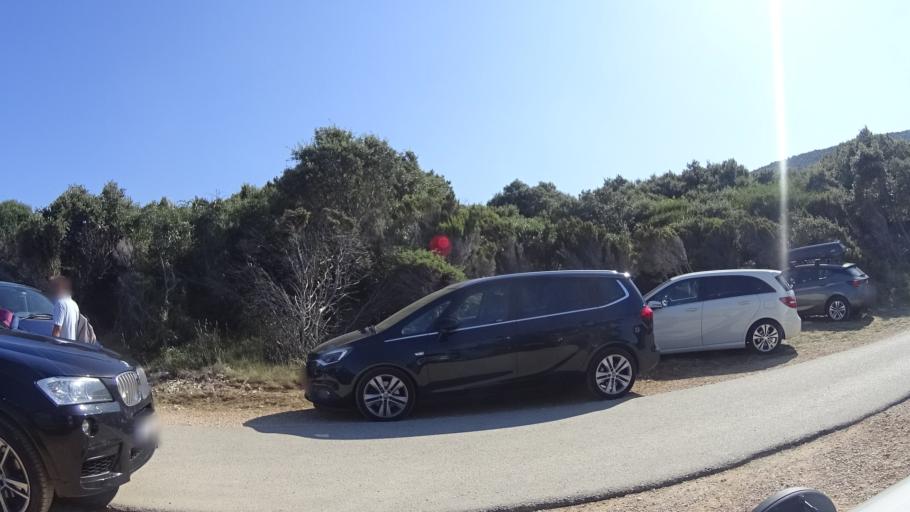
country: HR
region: Istarska
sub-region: Grad Labin
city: Rabac
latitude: 44.9964
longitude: 14.1693
